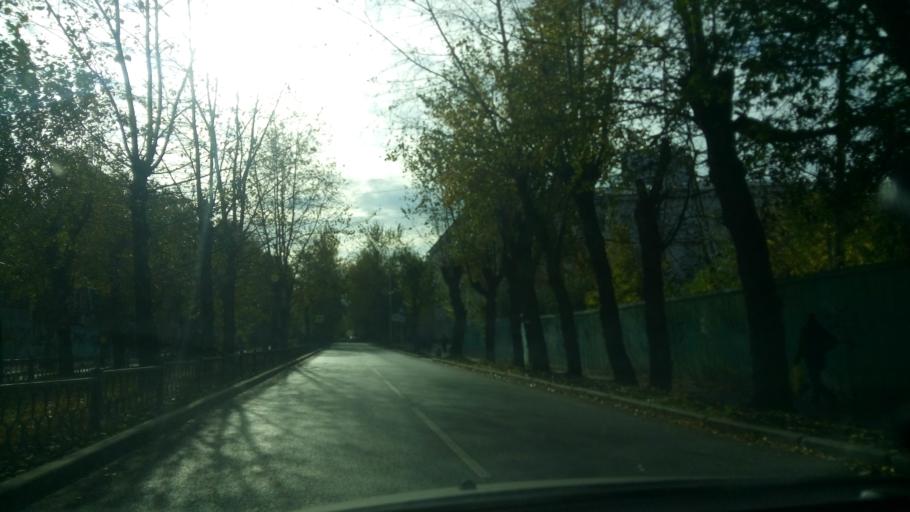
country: RU
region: Sverdlovsk
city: Yekaterinburg
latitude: 56.8892
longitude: 60.6201
